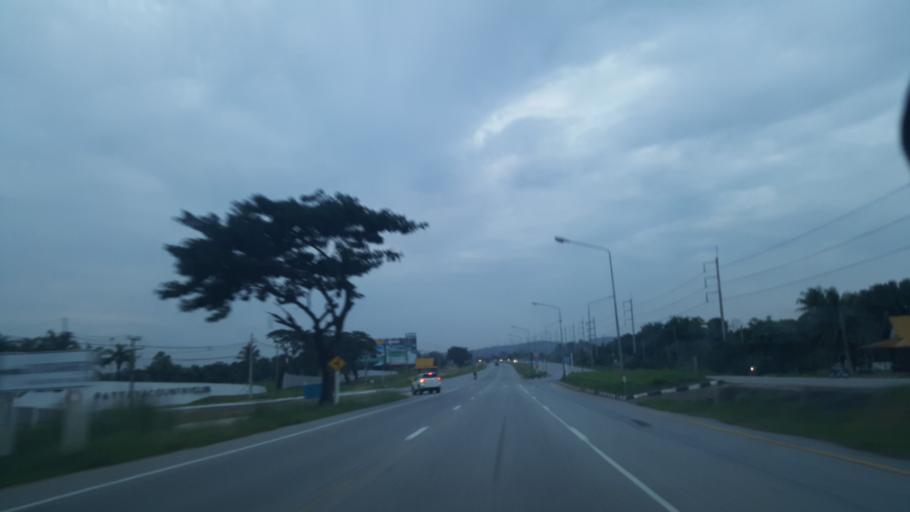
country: TH
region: Chon Buri
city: Ban Talat Bueng
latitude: 12.9250
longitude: 101.0339
